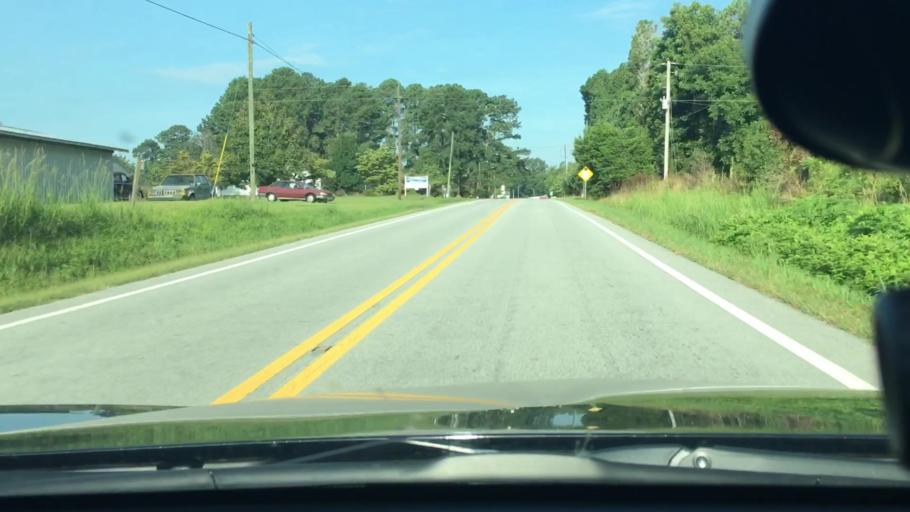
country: US
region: North Carolina
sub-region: Pitt County
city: Farmville
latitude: 35.6958
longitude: -77.5049
